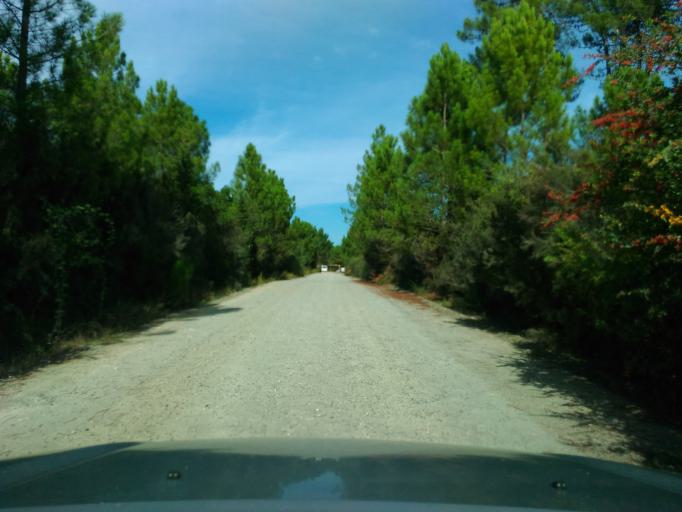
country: FR
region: Corsica
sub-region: Departement de la Haute-Corse
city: Ghisonaccia
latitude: 42.0115
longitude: 9.4585
